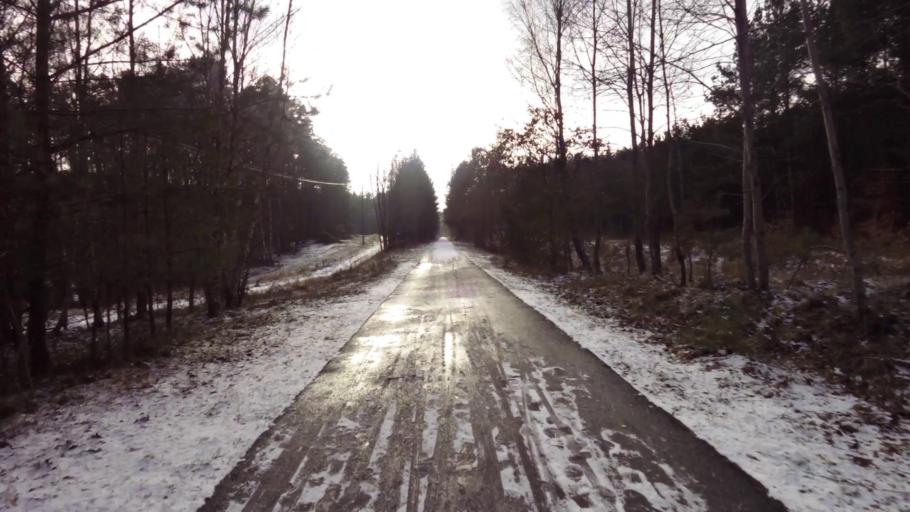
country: PL
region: West Pomeranian Voivodeship
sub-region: Powiat drawski
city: Zlocieniec
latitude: 53.5557
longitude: 16.0257
